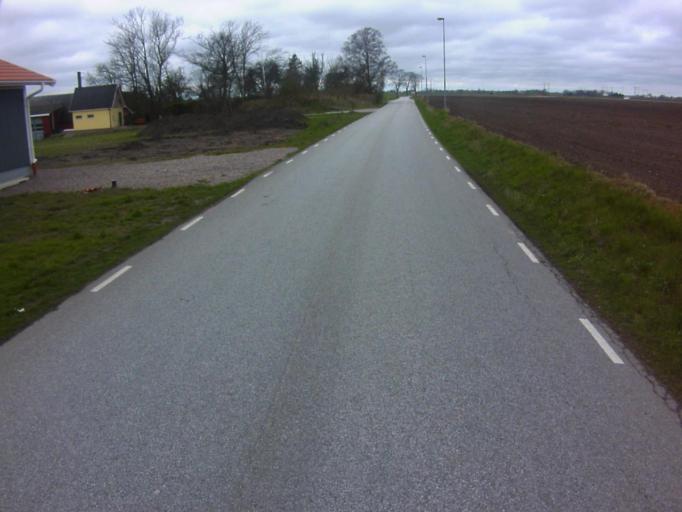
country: SE
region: Skane
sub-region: Kavlinge Kommun
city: Kaevlinge
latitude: 55.7943
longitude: 13.1957
